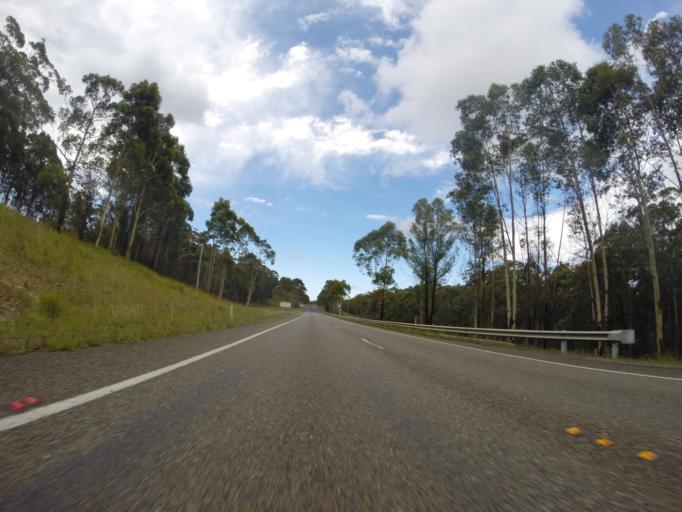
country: AU
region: New South Wales
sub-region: Shoalhaven Shire
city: Milton
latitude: -35.1302
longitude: 150.4684
